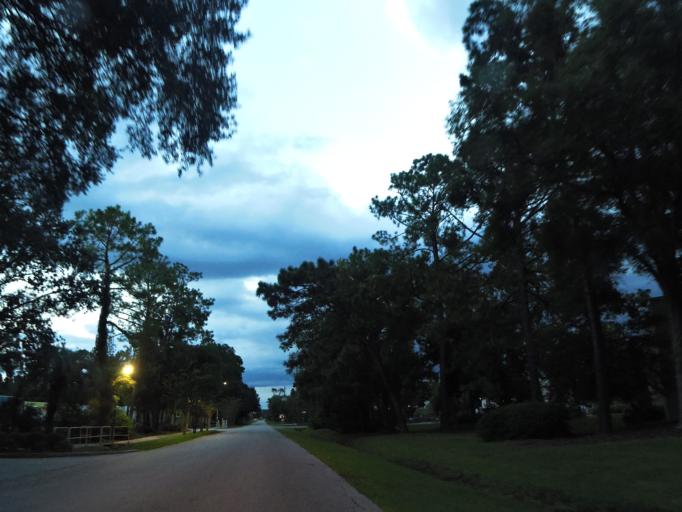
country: US
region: Florida
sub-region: Duval County
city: Jacksonville
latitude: 30.2606
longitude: -81.6080
